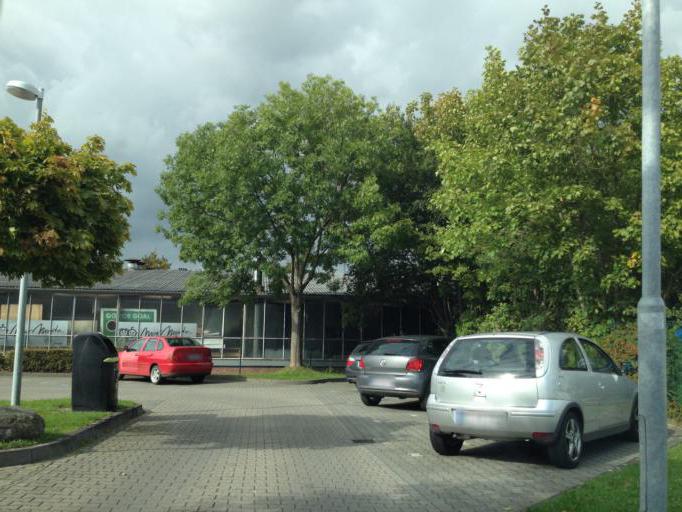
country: DE
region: North Rhine-Westphalia
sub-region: Regierungsbezirk Arnsberg
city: Soest
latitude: 51.5647
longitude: 8.0875
